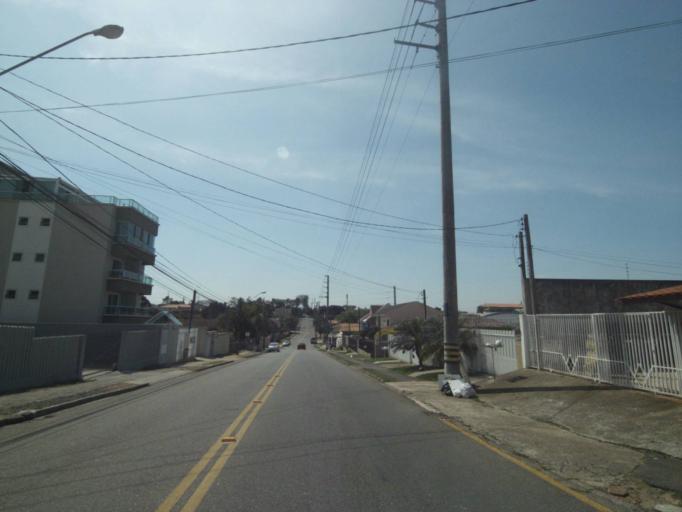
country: BR
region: Parana
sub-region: Curitiba
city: Curitiba
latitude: -25.4672
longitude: -49.3089
